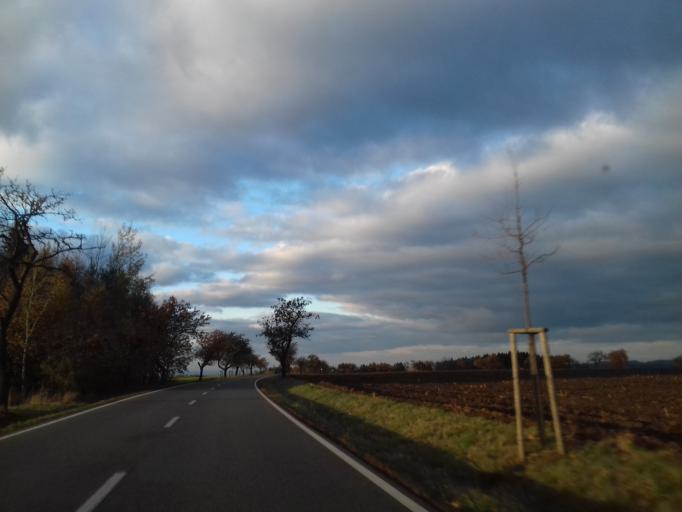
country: CZ
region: Pardubicky
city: Krouna
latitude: 49.8084
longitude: 16.0433
